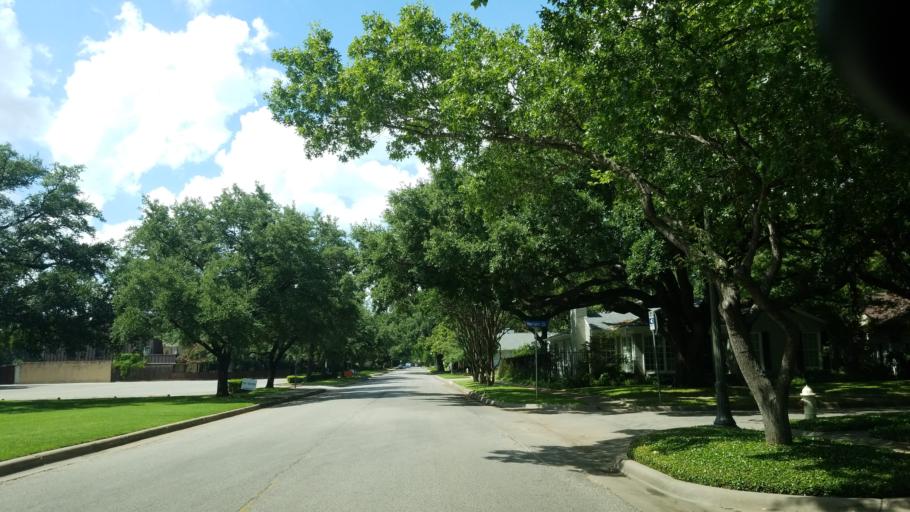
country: US
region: Texas
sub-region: Dallas County
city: Highland Park
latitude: 32.8294
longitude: -96.8191
